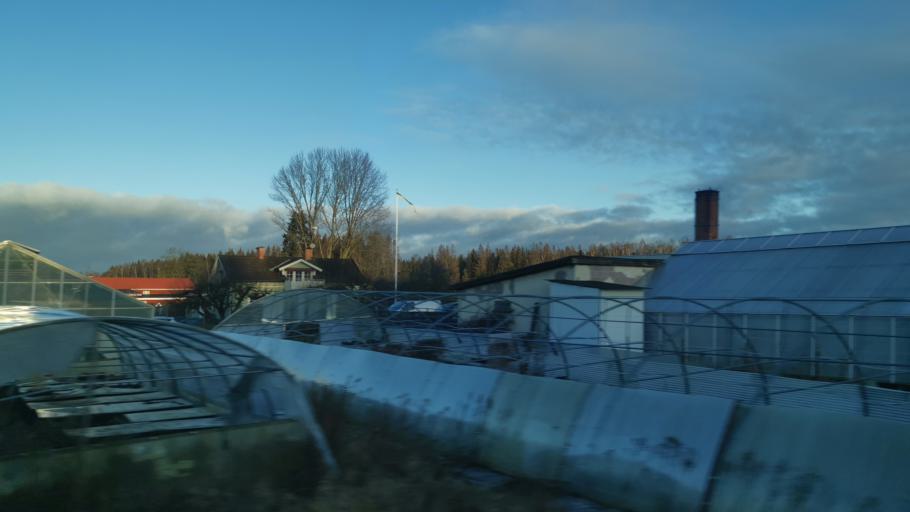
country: SE
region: Soedermanland
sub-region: Katrineholms Kommun
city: Katrineholm
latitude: 59.0084
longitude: 16.0845
